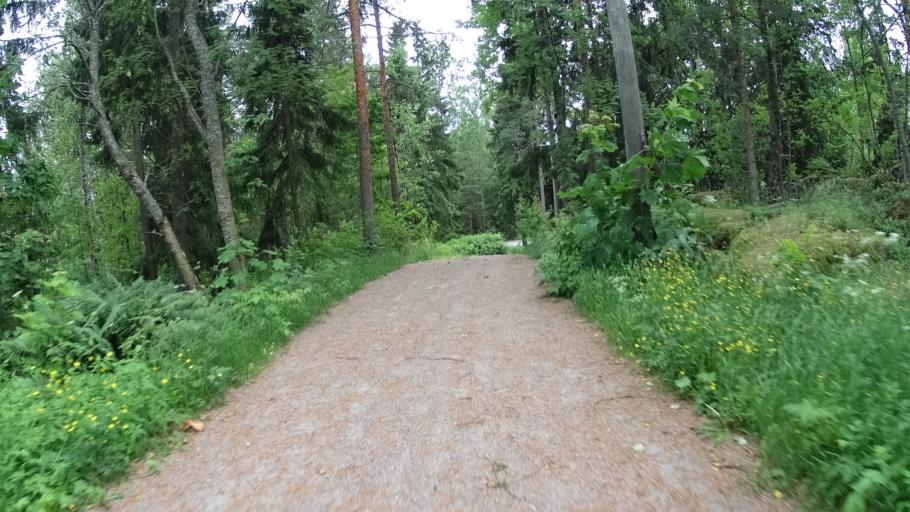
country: FI
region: Uusimaa
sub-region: Helsinki
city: Kauniainen
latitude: 60.1922
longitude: 24.7529
